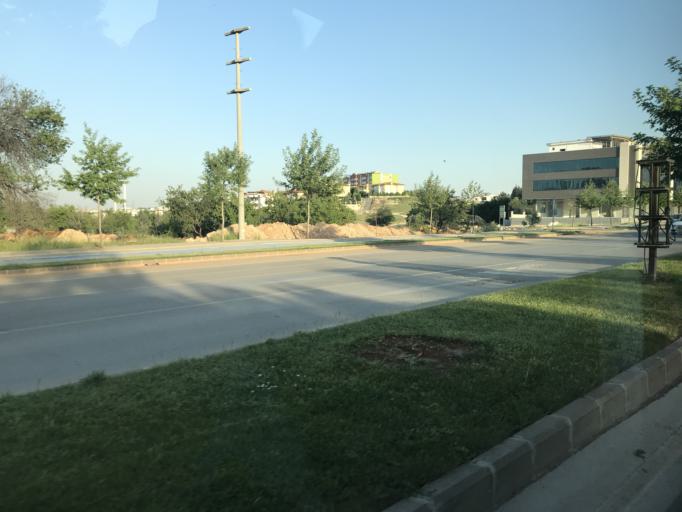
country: TR
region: Gaziantep
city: Sahinbey
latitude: 37.0615
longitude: 37.3206
